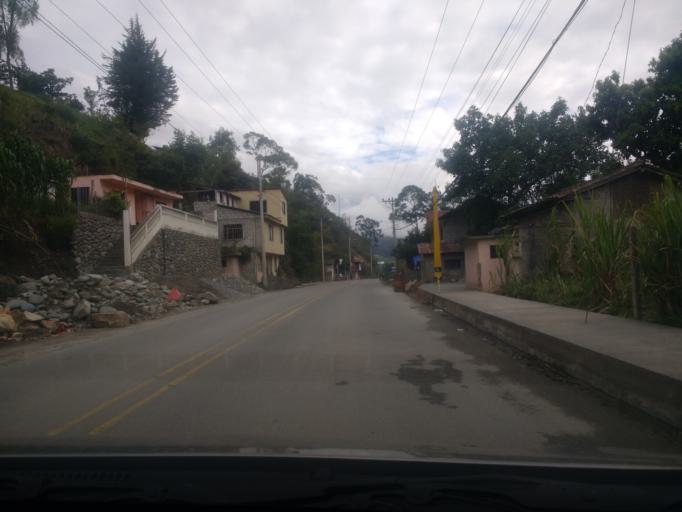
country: EC
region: Azuay
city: La Union
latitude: -2.8277
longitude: -78.7714
